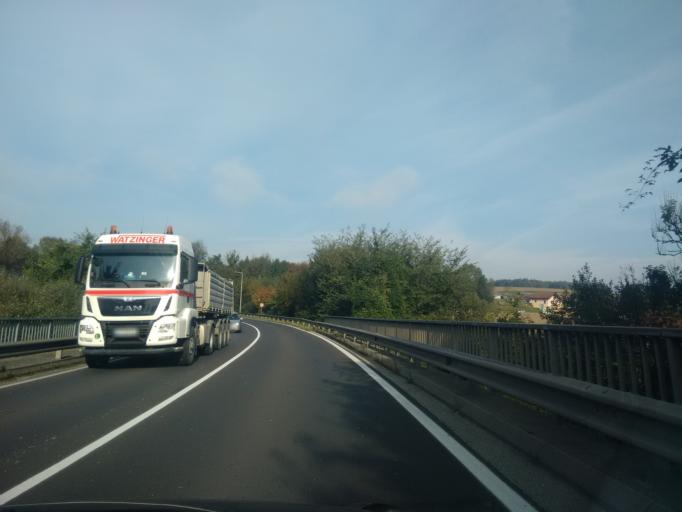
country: AT
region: Upper Austria
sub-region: Politischer Bezirk Grieskirchen
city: Bad Schallerbach
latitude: 48.2221
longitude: 13.9653
